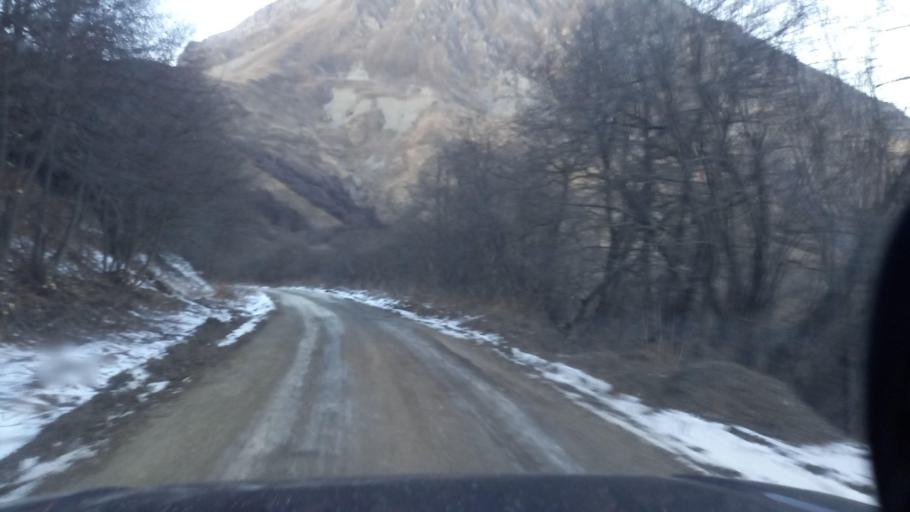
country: RU
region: Ingushetiya
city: Dzhayrakh
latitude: 42.8274
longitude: 44.5752
